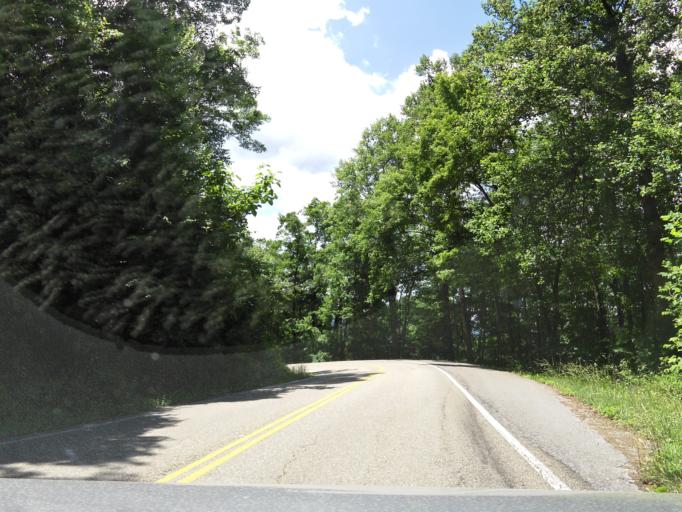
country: US
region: North Carolina
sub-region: Graham County
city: Robbinsville
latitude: 35.5041
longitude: -83.9479
